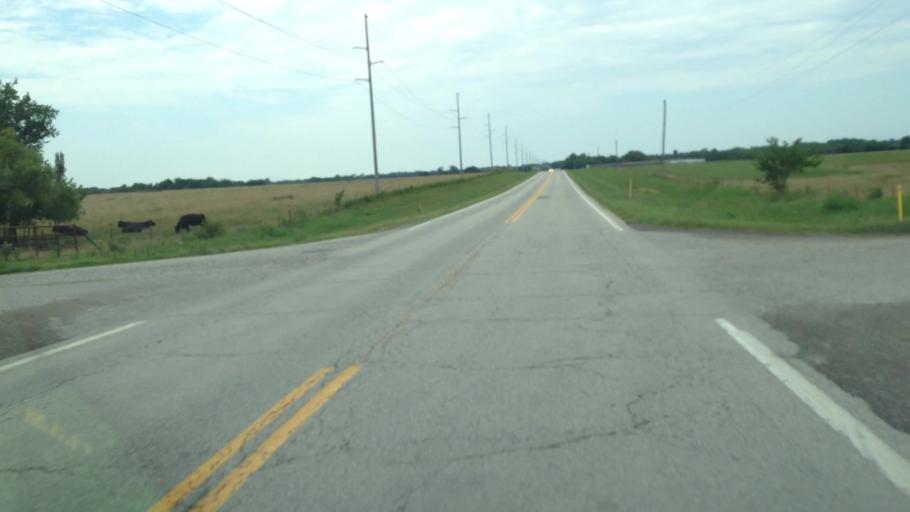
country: US
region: Kansas
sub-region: Labette County
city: Chetopa
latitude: 36.9172
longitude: -95.0896
